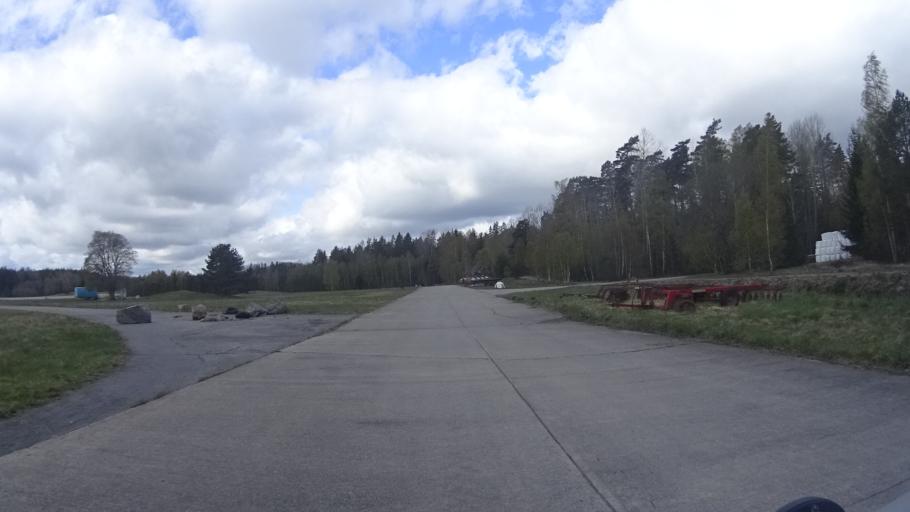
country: SE
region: Stockholm
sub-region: Botkyrka Kommun
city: Tullinge
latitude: 59.1775
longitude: 17.8957
